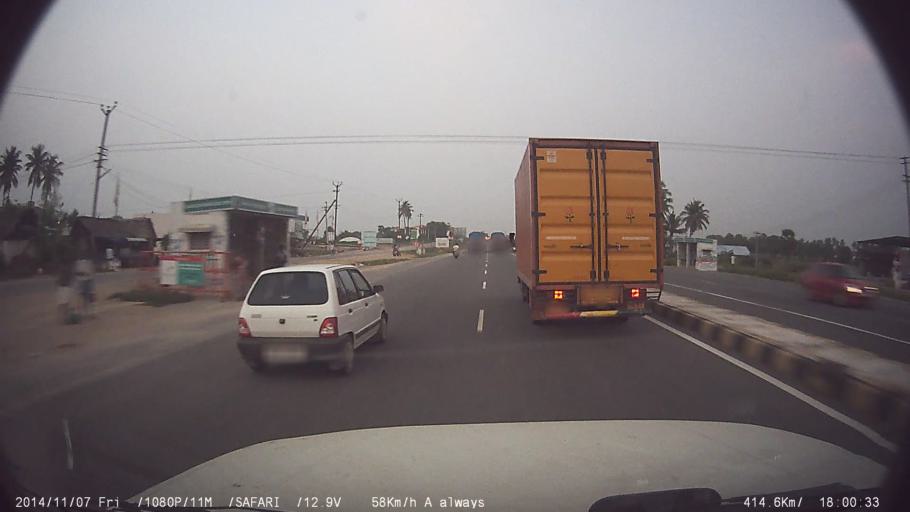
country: IN
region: Tamil Nadu
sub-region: Erode
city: Erode
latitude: 11.3703
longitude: 77.6485
